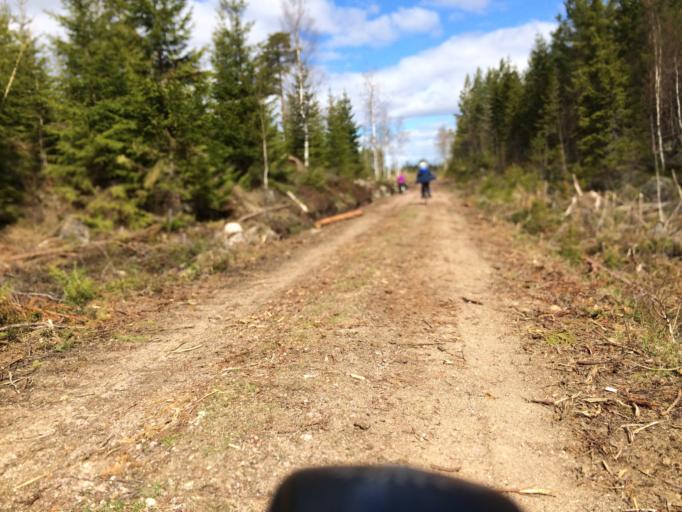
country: SE
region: OErebro
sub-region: Hallefors Kommun
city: Haellefors
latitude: 60.0485
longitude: 14.5260
